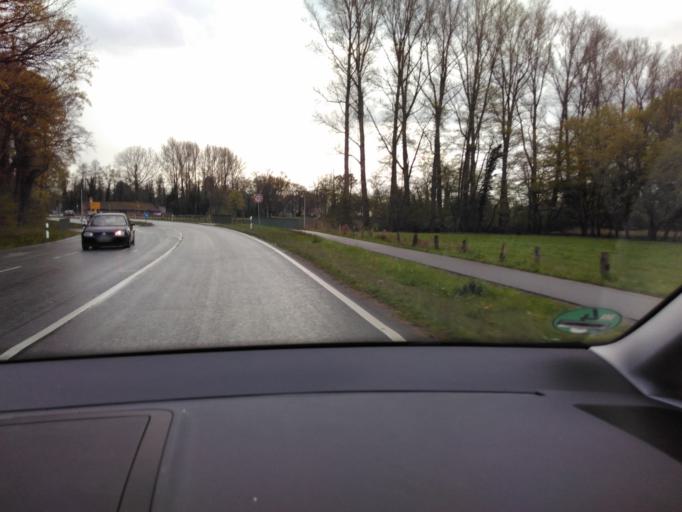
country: DE
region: North Rhine-Westphalia
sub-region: Regierungsbezirk Detmold
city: Verl
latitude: 51.8888
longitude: 8.5082
